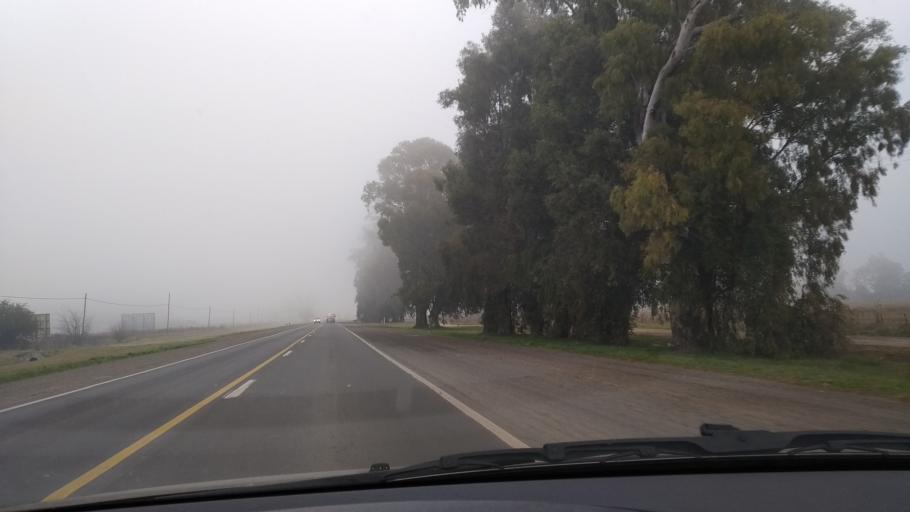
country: AR
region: Buenos Aires
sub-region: Partido de Azul
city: Azul
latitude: -36.7988
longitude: -59.8485
